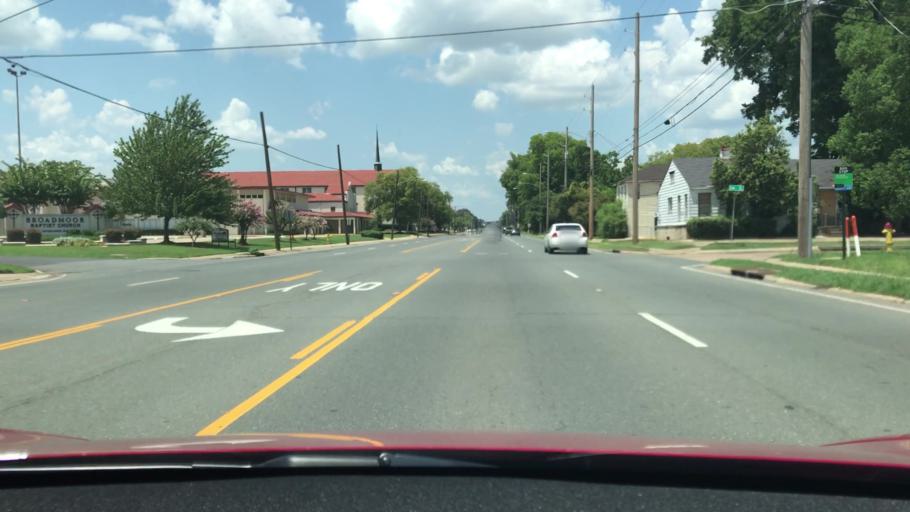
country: US
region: Louisiana
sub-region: Bossier Parish
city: Bossier City
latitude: 32.4621
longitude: -93.7221
